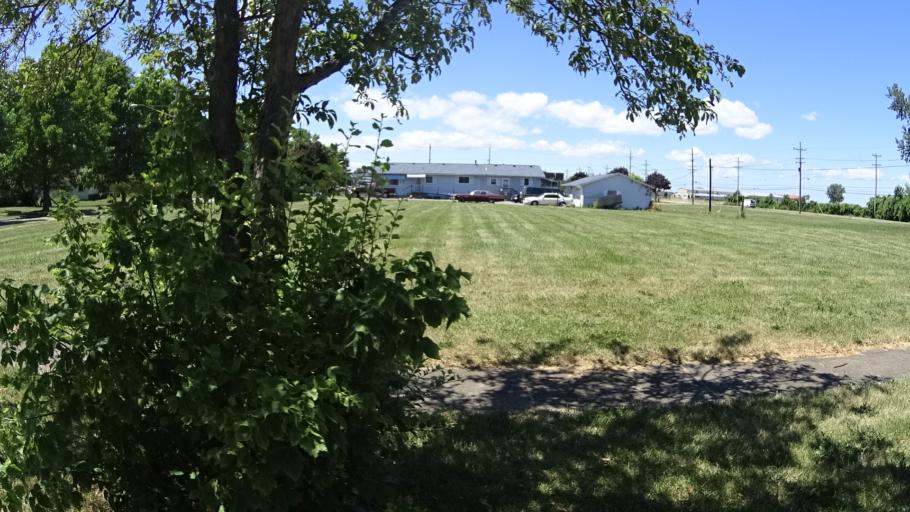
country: US
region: Ohio
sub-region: Erie County
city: Sandusky
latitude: 41.4503
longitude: -82.6803
